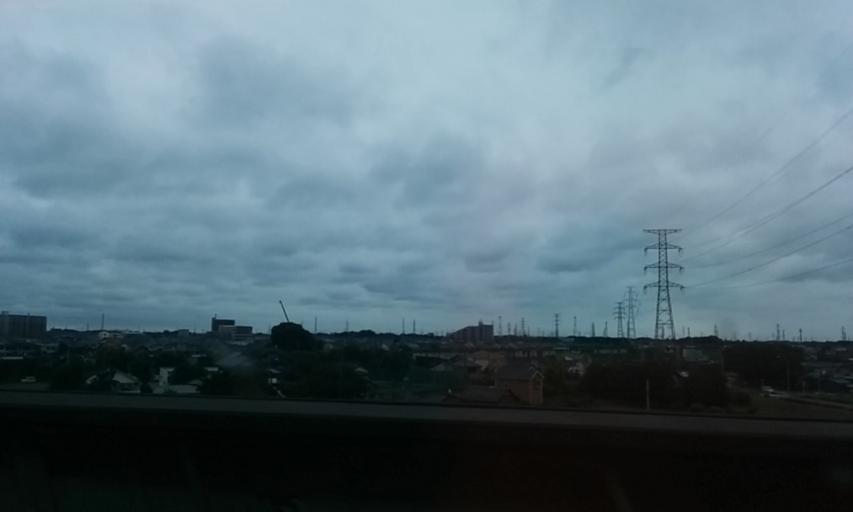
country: JP
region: Saitama
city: Shiraoka
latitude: 36.0347
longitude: 139.6623
